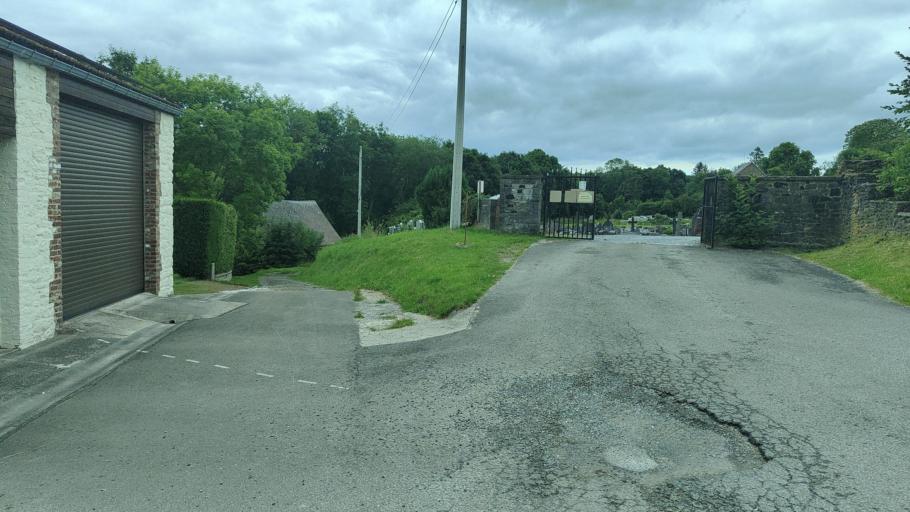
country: BE
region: Wallonia
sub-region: Province du Hainaut
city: Chimay
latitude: 50.0513
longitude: 4.3190
